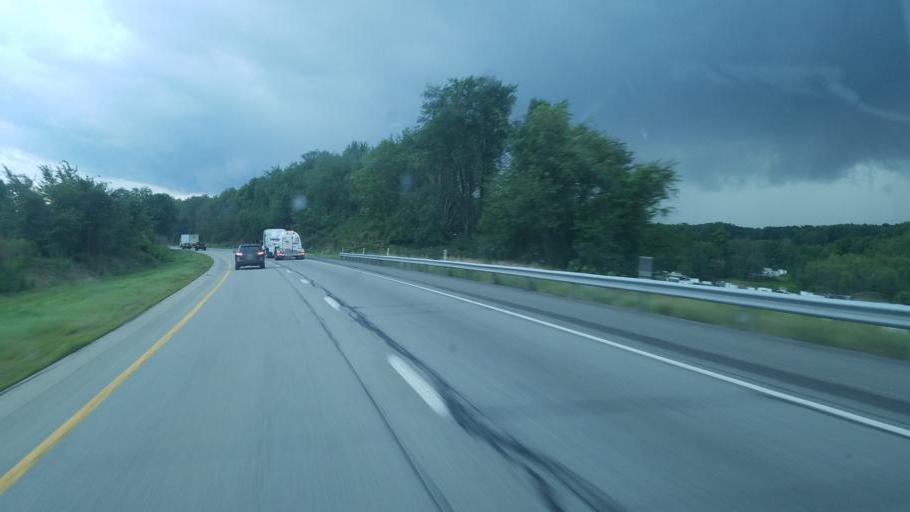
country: US
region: Pennsylvania
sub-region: Butler County
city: Slippery Rock
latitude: 40.9874
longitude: -80.1326
